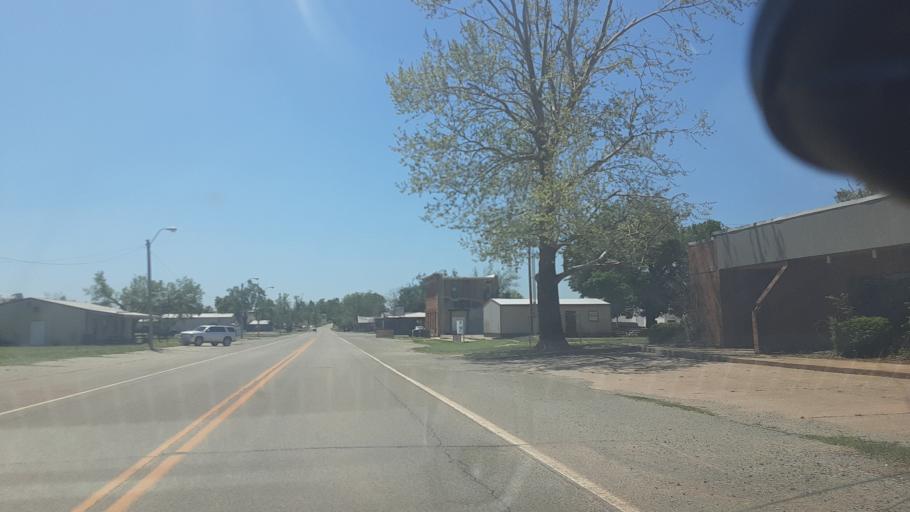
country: US
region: Oklahoma
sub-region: Logan County
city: Guthrie
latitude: 36.0658
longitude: -97.4071
